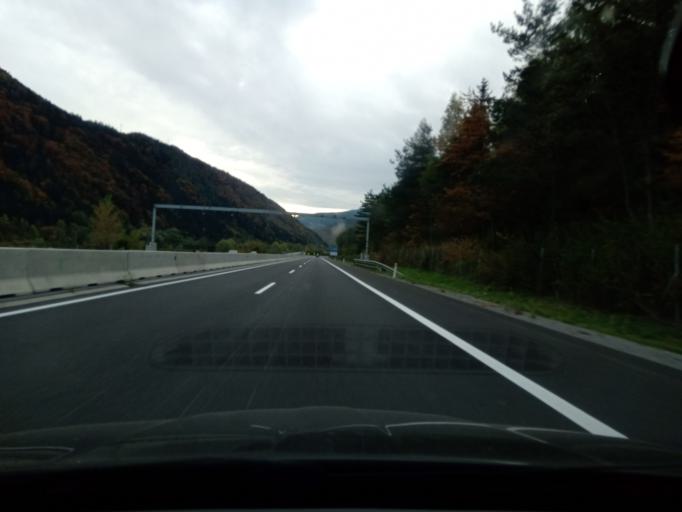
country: AT
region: Styria
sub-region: Politischer Bezirk Graz-Umgebung
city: Schrems bei Frohnleiten
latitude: 47.2966
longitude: 15.3409
